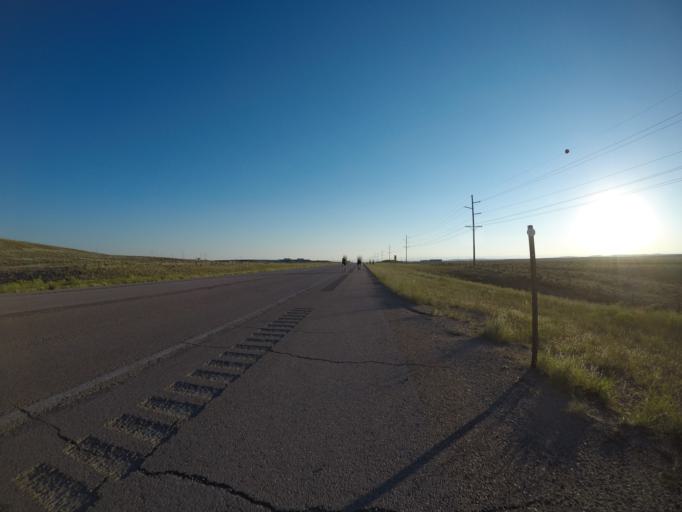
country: US
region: Wyoming
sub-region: Sublette County
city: Marbleton
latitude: 42.5763
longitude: -110.0929
